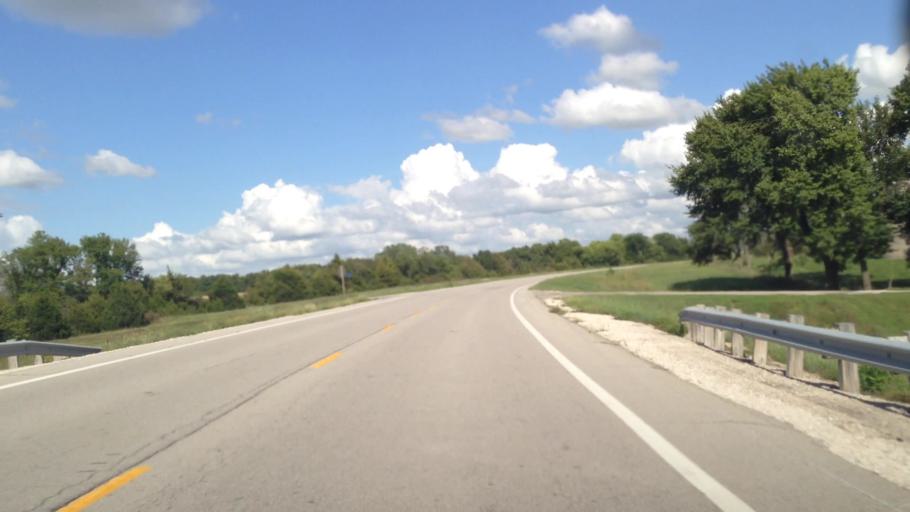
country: US
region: Kansas
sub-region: Neosho County
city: Erie
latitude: 37.6880
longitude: -95.2353
